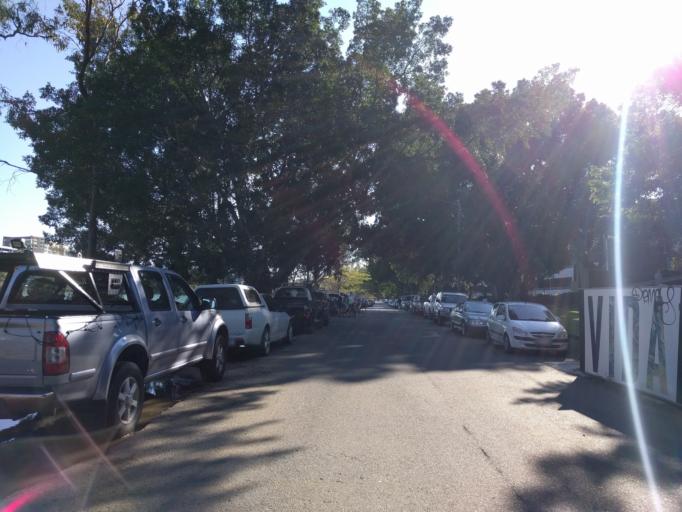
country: AU
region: Queensland
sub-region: Brisbane
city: Milton
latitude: -27.4754
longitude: 153.0063
